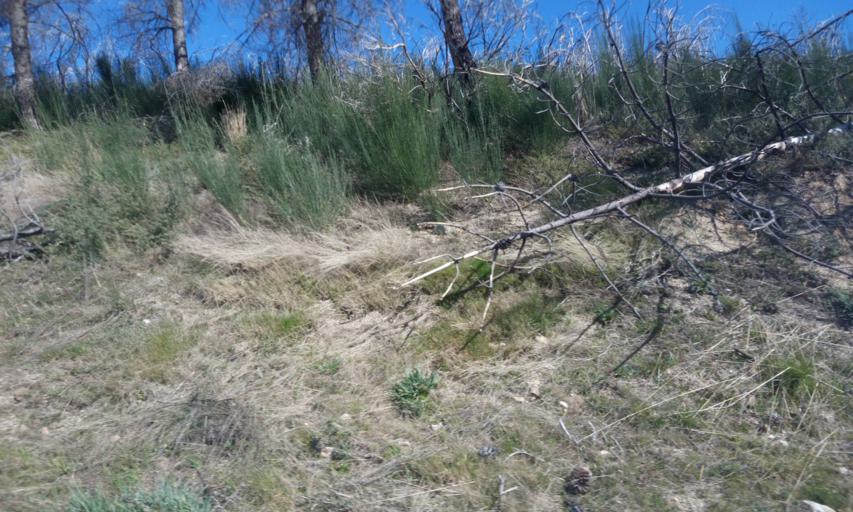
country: PT
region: Guarda
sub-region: Manteigas
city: Manteigas
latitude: 40.4883
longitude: -7.5513
